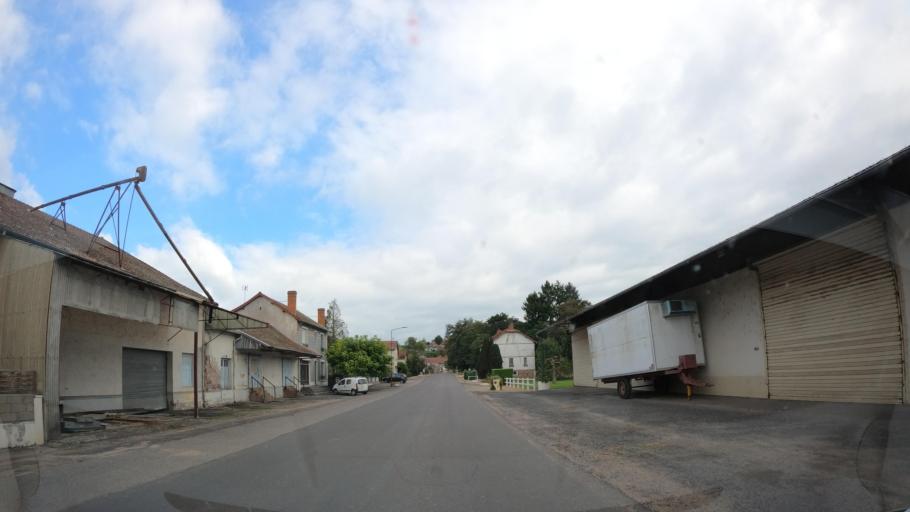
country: FR
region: Auvergne
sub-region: Departement de l'Allier
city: Lapalisse
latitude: 46.3276
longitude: 3.5910
